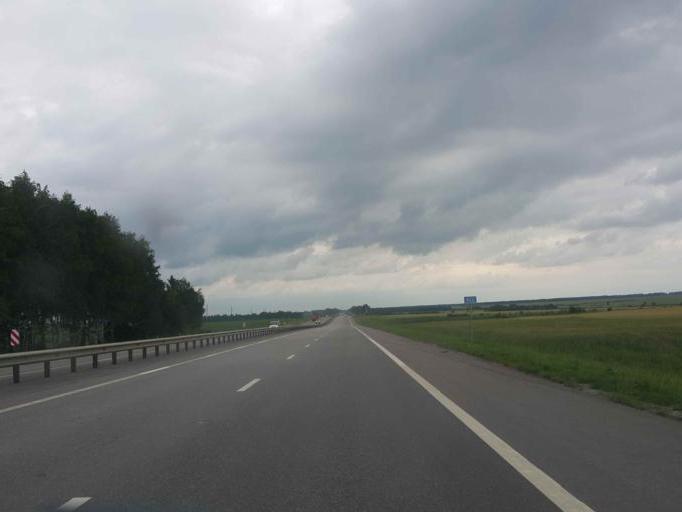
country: RU
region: Tambov
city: Selezni
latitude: 52.8205
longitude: 40.9261
